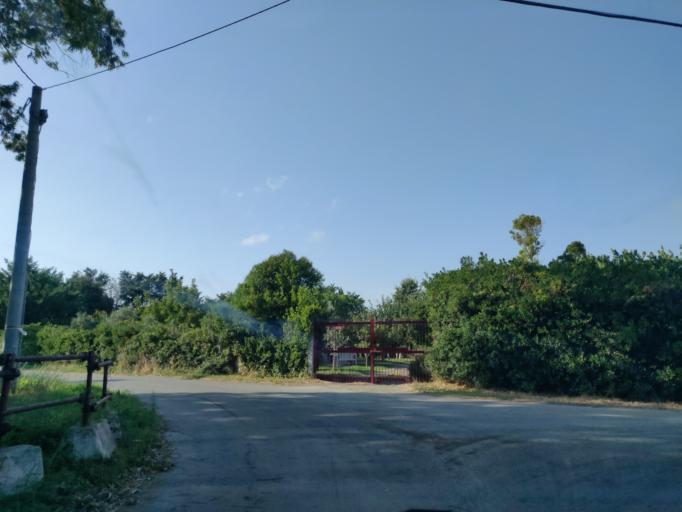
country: IT
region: Latium
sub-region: Citta metropolitana di Roma Capitale
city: Aurelia
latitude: 42.1367
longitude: 11.7602
